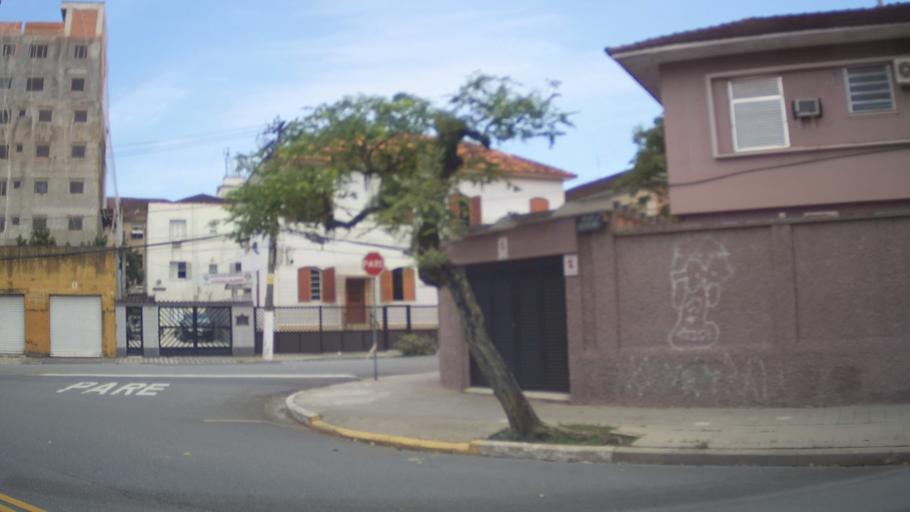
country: BR
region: Sao Paulo
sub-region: Santos
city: Santos
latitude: -23.9512
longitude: -46.3405
